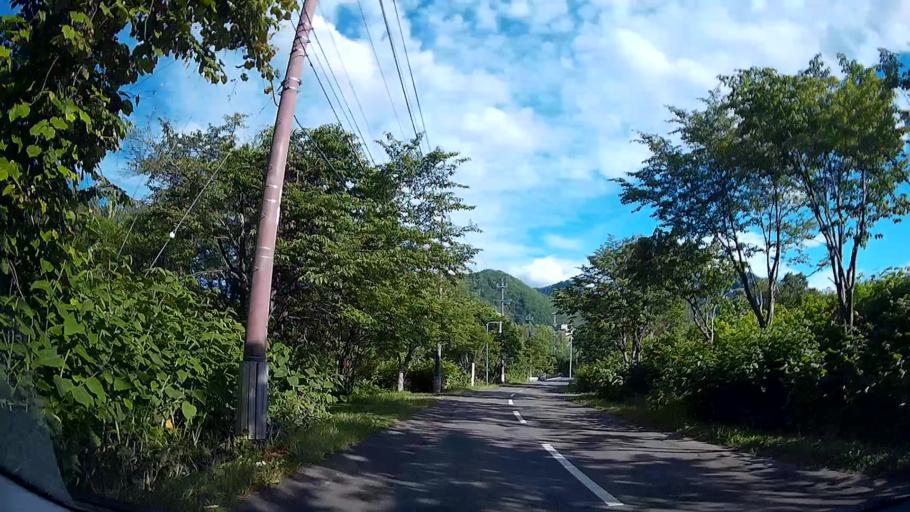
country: JP
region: Hokkaido
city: Sapporo
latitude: 42.9751
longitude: 141.1656
